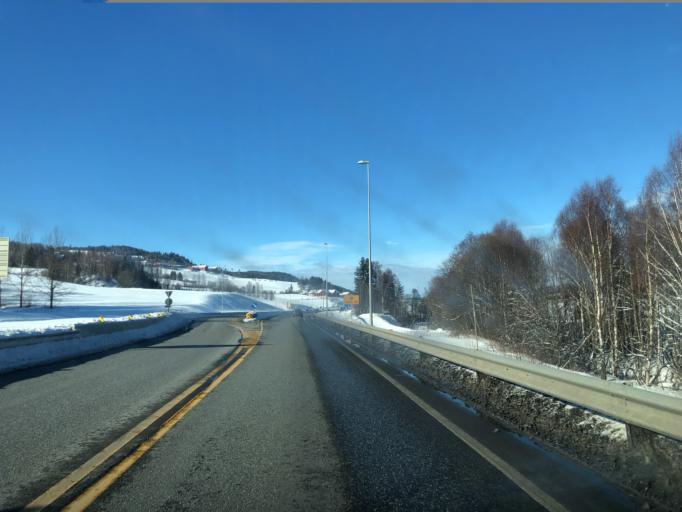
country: NO
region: Oppland
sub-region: Lunner
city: Roa
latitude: 60.3231
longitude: 10.5806
